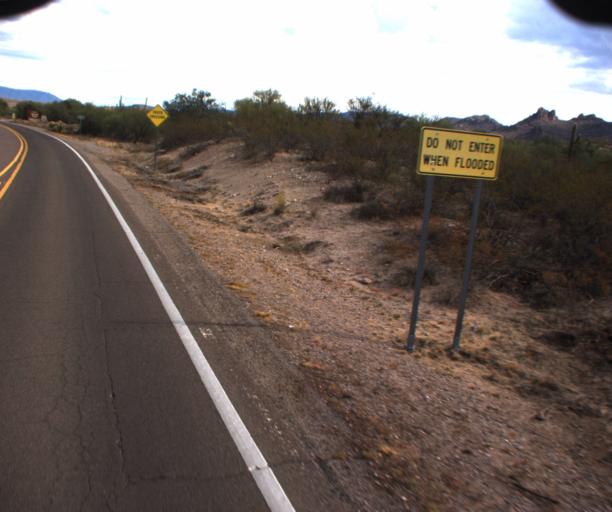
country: US
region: Arizona
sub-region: Pinal County
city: Apache Junction
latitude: 33.4653
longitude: -111.4808
